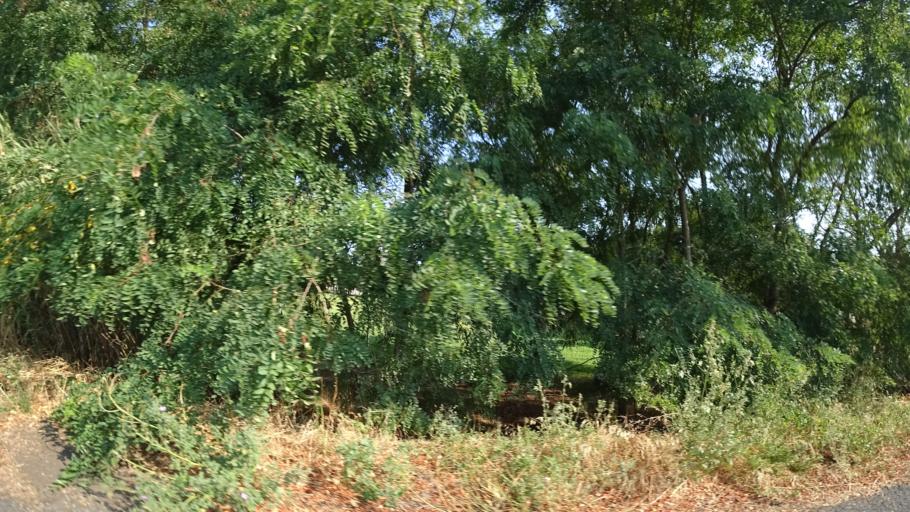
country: FR
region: Languedoc-Roussillon
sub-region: Departement des Pyrenees-Orientales
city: Bompas
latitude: 42.7148
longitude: 2.9296
